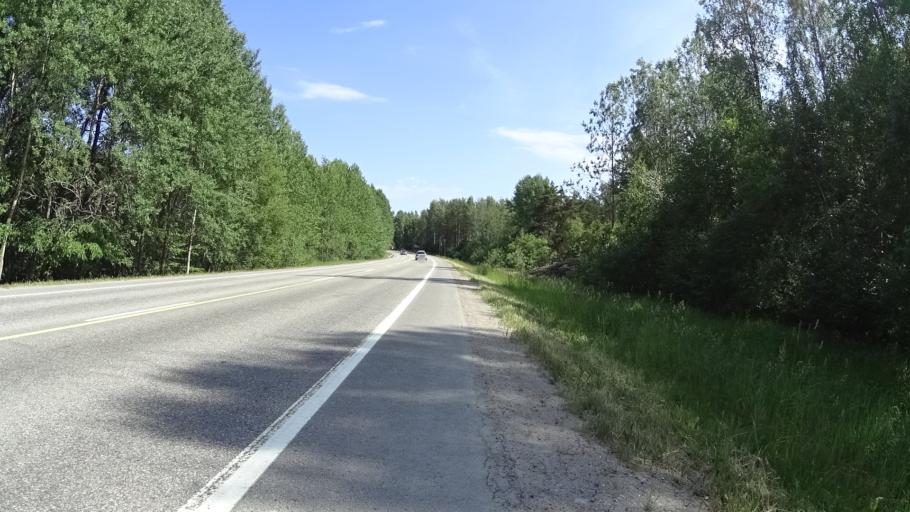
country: FI
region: Uusimaa
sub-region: Raaseporin
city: Karis
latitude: 60.0895
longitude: 23.6449
